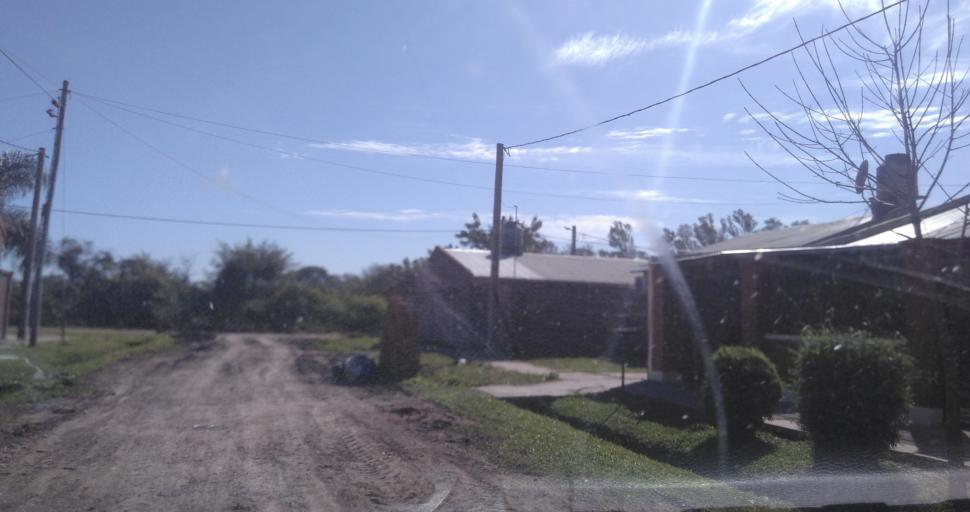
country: AR
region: Chaco
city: Fontana
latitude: -27.4382
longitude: -59.0267
